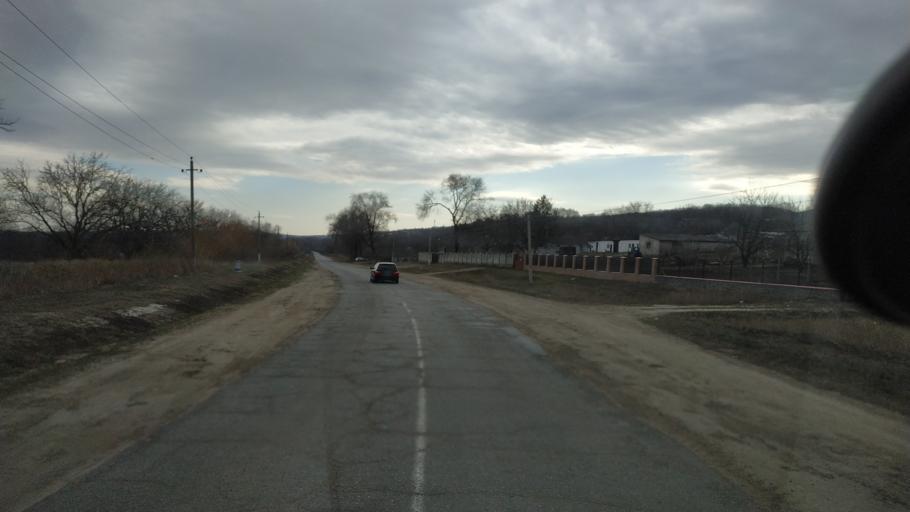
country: MD
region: Chisinau
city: Vadul lui Voda
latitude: 47.1382
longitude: 29.0609
